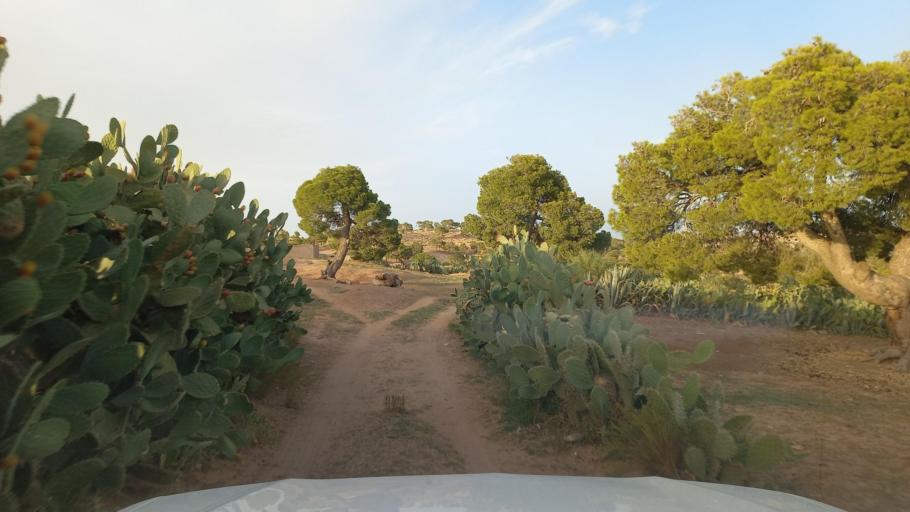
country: TN
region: Al Qasrayn
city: Sbiba
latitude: 35.4133
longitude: 8.9080
